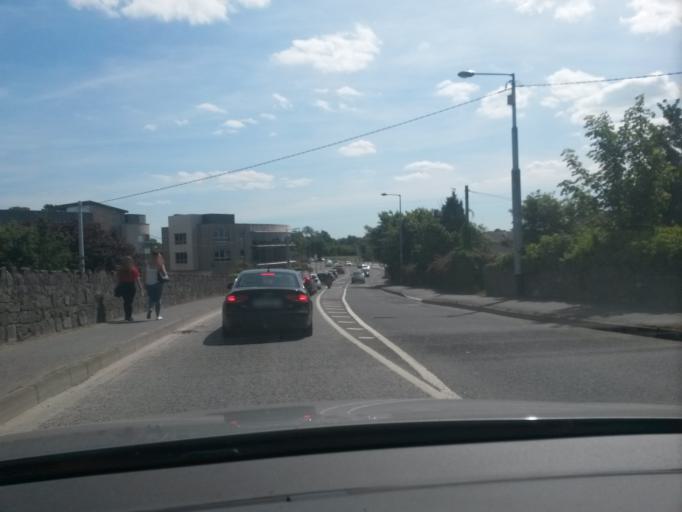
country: IE
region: Leinster
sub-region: Kildare
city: Sallins
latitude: 53.2464
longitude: -6.6656
